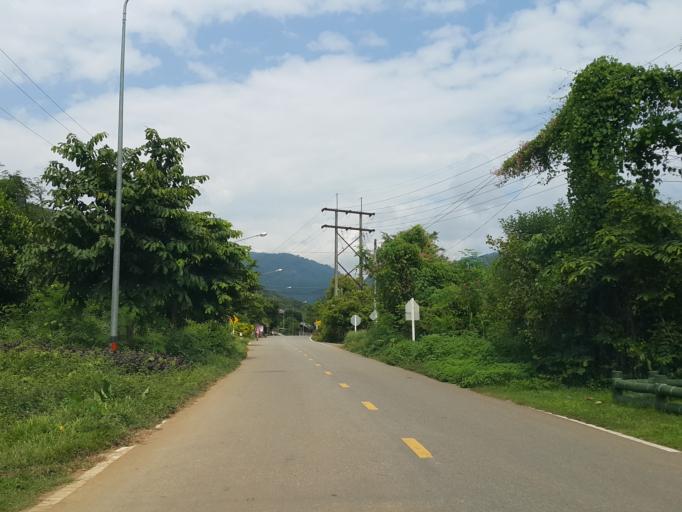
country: TH
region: Mae Hong Son
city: Mae Hong Son
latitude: 19.4678
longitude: 97.9675
